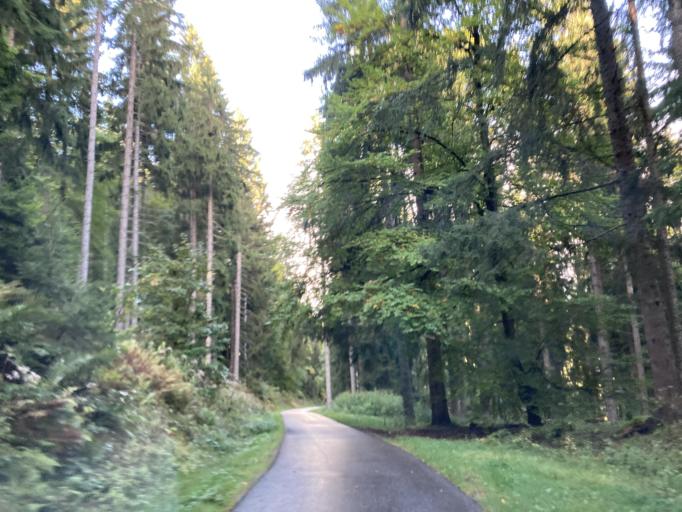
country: DE
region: Baden-Wuerttemberg
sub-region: Freiburg Region
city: Triberg im Schwarzwald
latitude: 48.1061
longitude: 8.2568
